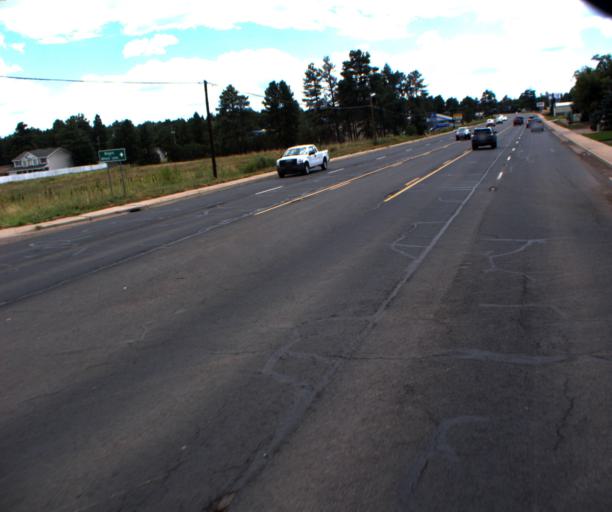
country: US
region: Arizona
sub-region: Navajo County
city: Lake of the Woods
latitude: 34.1910
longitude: -110.0157
